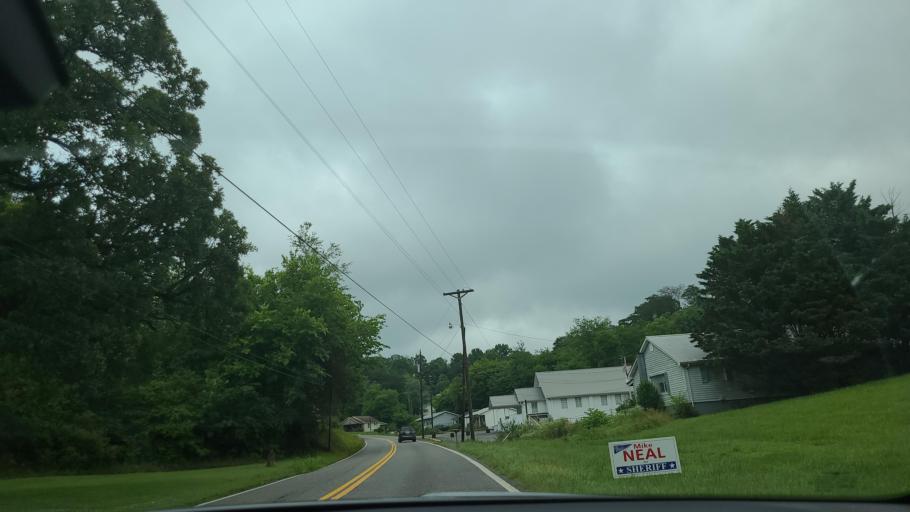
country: US
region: Tennessee
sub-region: Rhea County
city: Dayton
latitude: 35.5008
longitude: -84.9869
